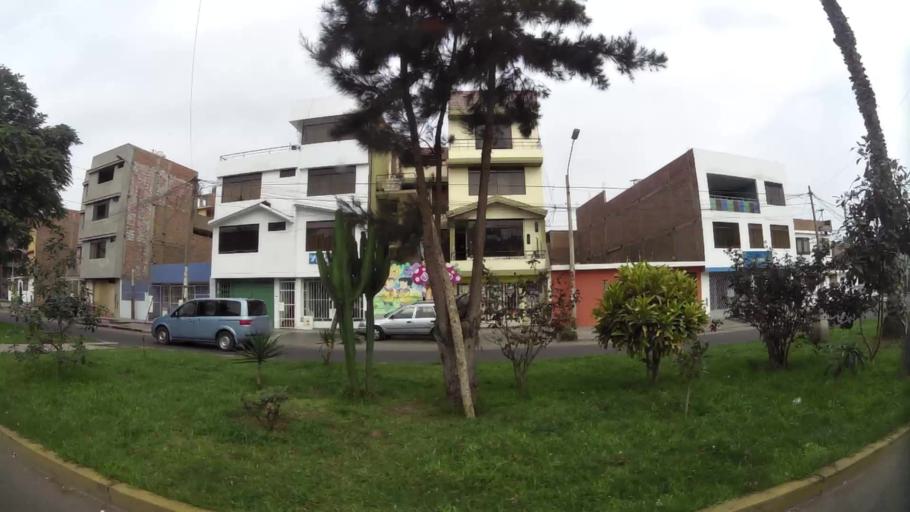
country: PE
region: Lima
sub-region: Lima
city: Independencia
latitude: -12.0139
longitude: -77.0880
